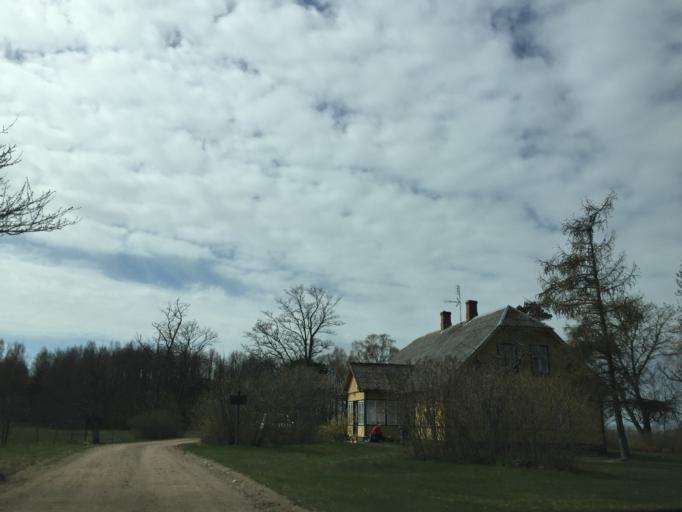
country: LV
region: Salacgrivas
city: Salacgriva
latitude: 57.5892
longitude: 24.3716
